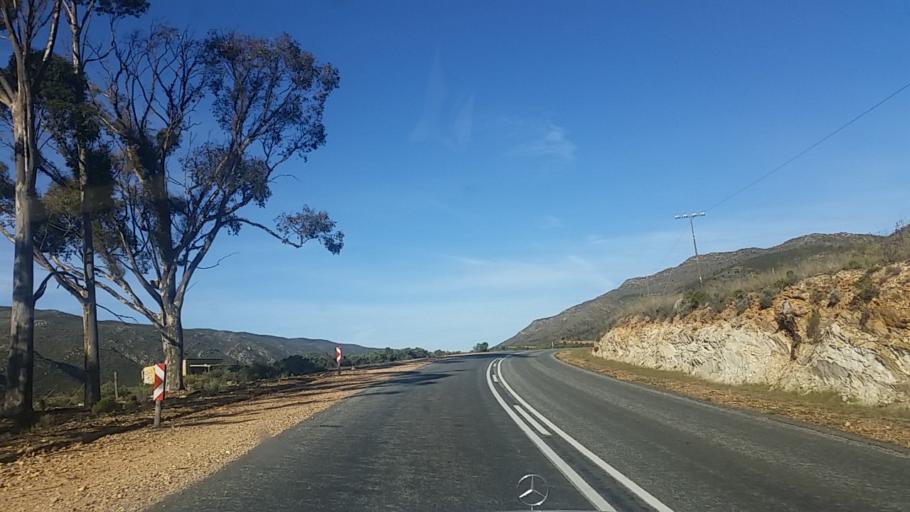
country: ZA
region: Western Cape
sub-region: Eden District Municipality
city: Knysna
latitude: -33.7521
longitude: 22.9510
